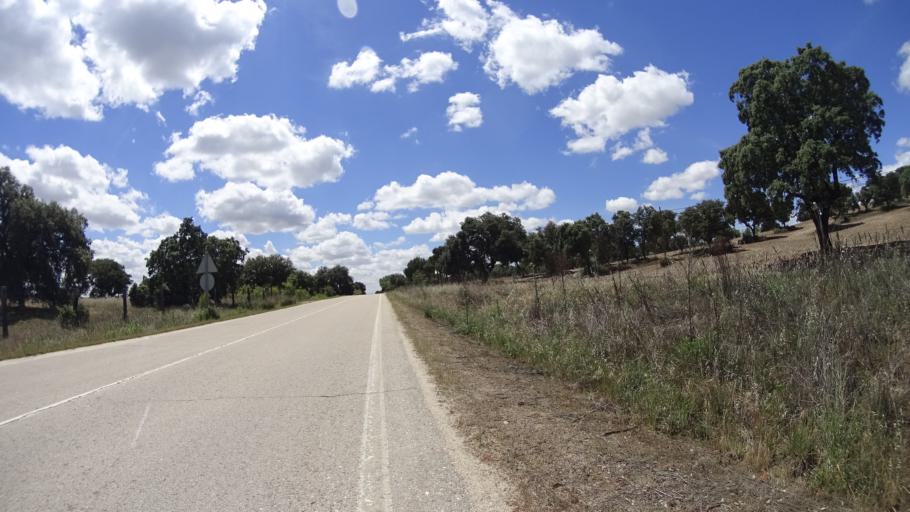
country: ES
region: Madrid
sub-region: Provincia de Madrid
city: Villanueva del Pardillo
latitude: 40.4499
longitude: -3.9533
